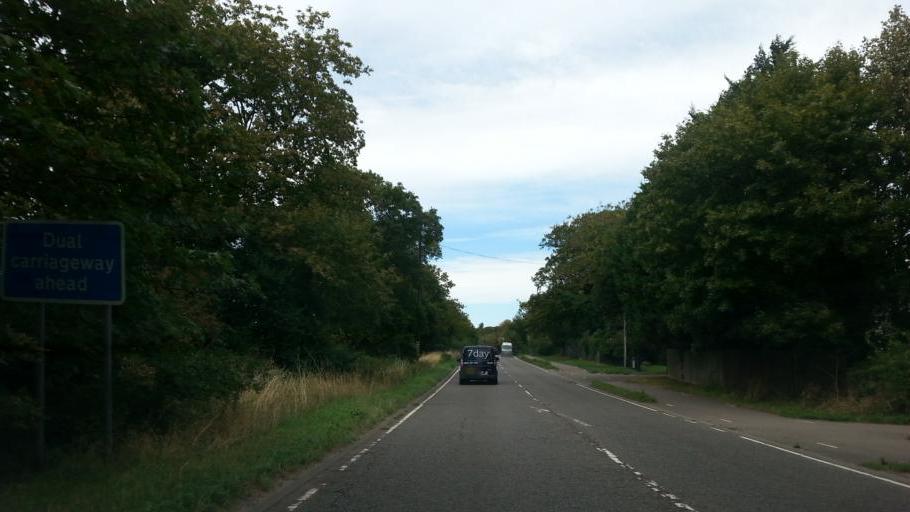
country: GB
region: England
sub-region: Cambridgeshire
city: Sawston
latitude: 52.1521
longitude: 0.1883
